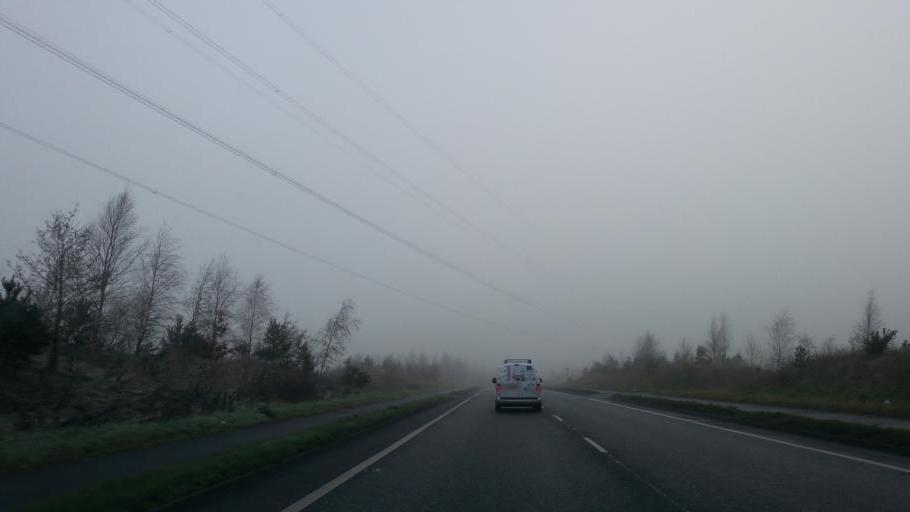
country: GB
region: England
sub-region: Cheshire East
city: Alderley Edge
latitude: 53.2878
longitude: -2.2523
